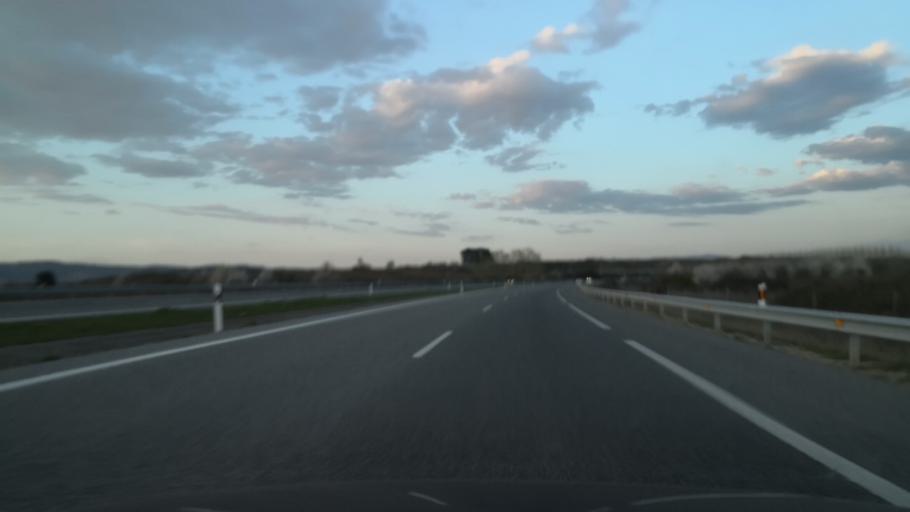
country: ES
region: Castille and Leon
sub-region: Provincia de Leon
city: Cacabelos
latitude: 42.5770
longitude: -6.7096
